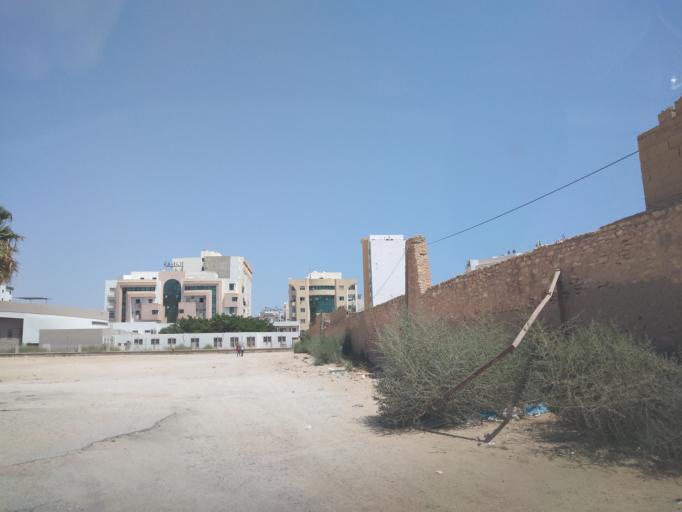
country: TN
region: Safaqis
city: Sfax
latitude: 34.7355
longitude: 10.7501
